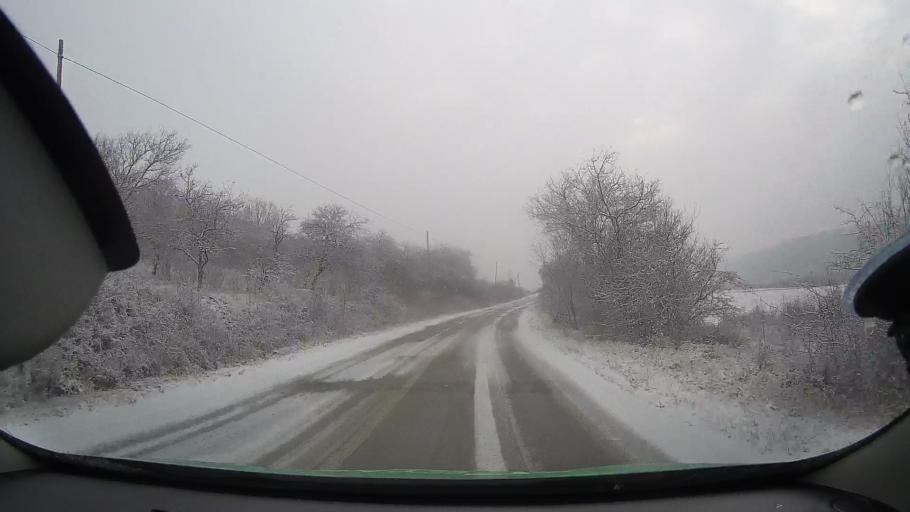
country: RO
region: Alba
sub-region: Municipiul Aiud
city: Aiudul de Sus
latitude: 46.3354
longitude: 23.6717
